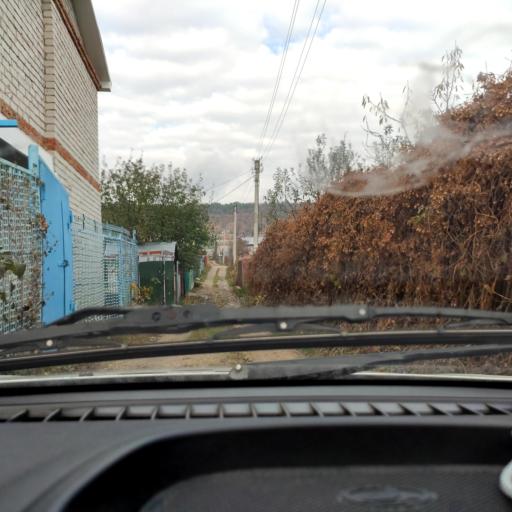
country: RU
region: Samara
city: Zhigulevsk
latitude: 53.4645
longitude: 49.6428
